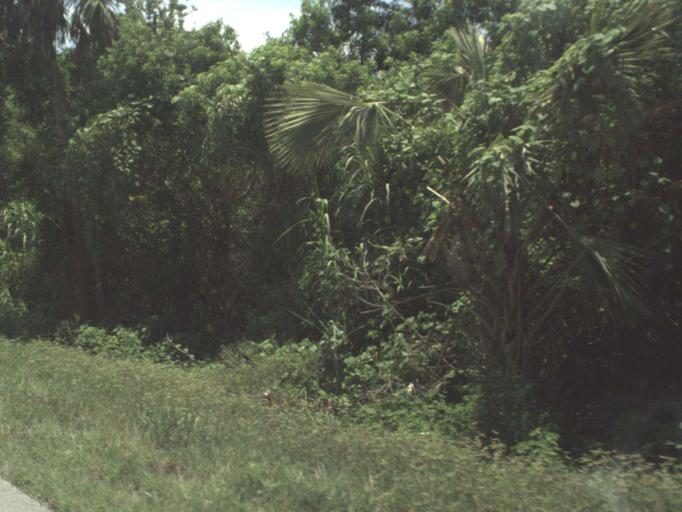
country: US
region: Florida
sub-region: Martin County
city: Indiantown
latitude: 26.9679
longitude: -80.6110
